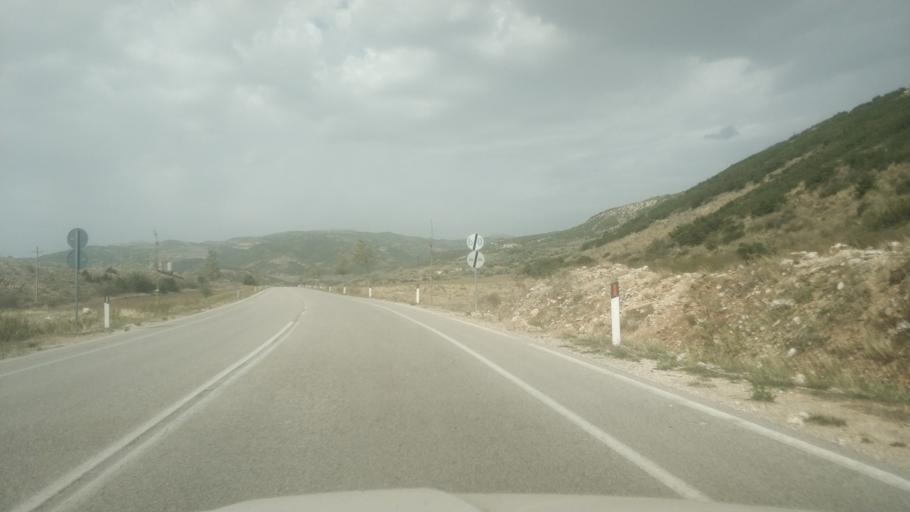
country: AL
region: Gjirokaster
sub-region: Rrethi i Tepelenes
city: Memaliaj
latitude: 40.3673
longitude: 19.9086
